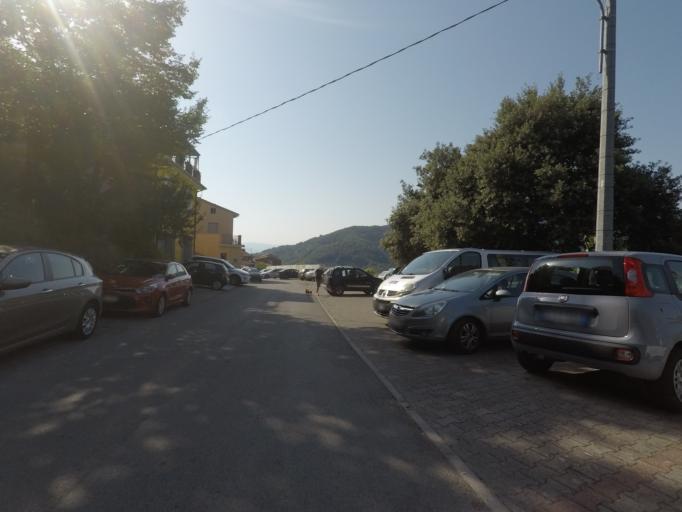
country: IT
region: Liguria
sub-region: Provincia di La Spezia
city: Casano-Dogana-Isola
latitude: 44.0891
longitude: 10.0557
